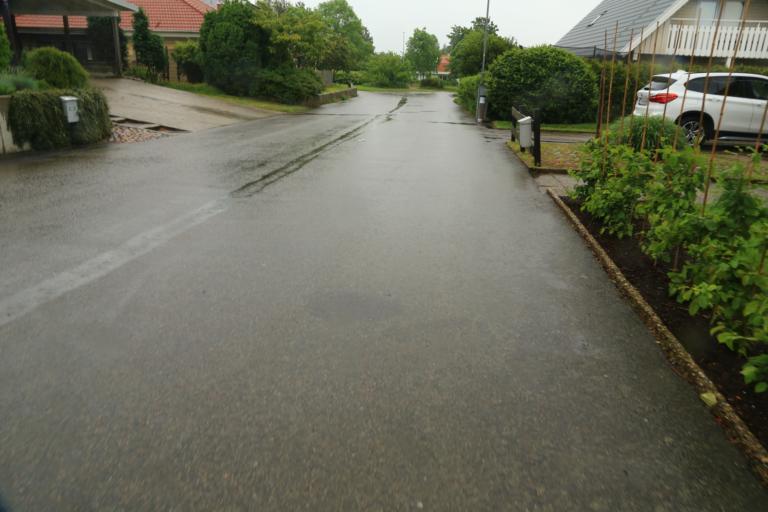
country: SE
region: Halland
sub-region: Varbergs Kommun
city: Varberg
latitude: 57.1028
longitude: 12.2870
